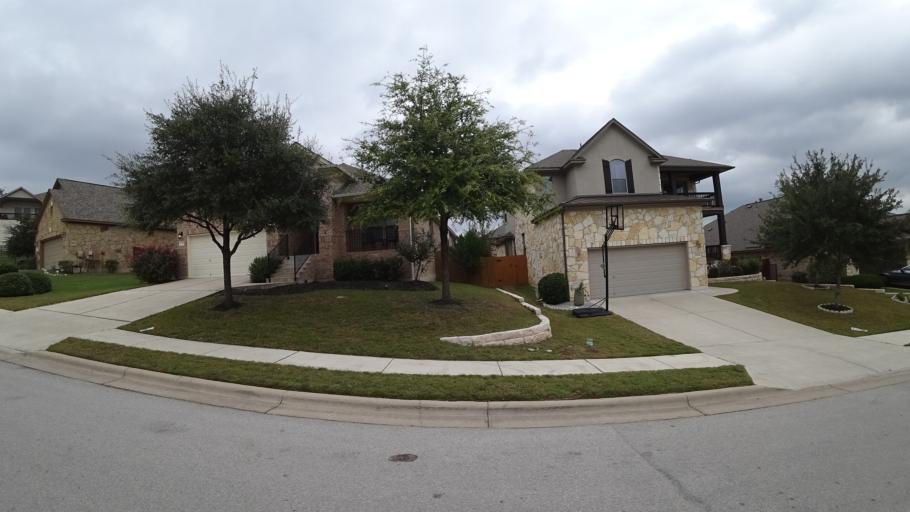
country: US
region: Texas
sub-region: Travis County
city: Bee Cave
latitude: 30.3426
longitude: -97.9155
